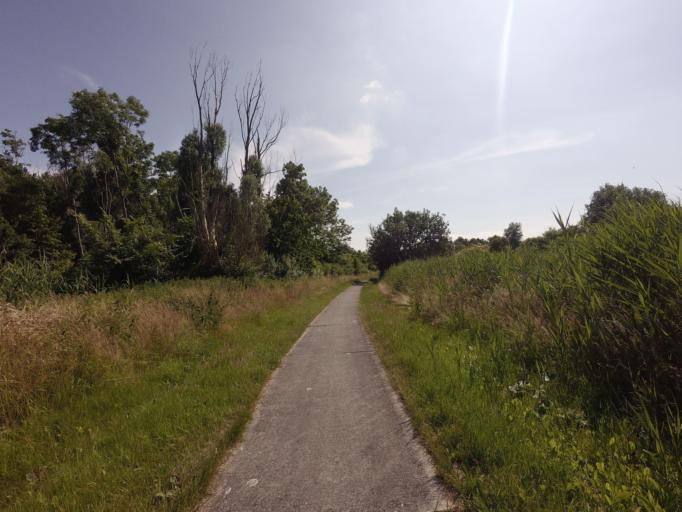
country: NL
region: Flevoland
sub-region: Gemeente Lelystad
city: Lelystad
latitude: 52.4245
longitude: 5.4161
